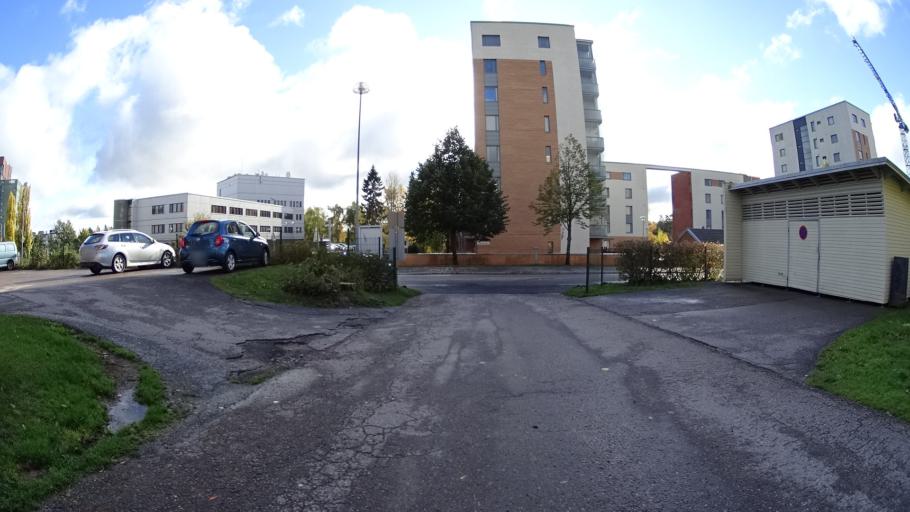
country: FI
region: Uusimaa
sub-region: Helsinki
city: Teekkarikylae
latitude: 60.2777
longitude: 24.8500
